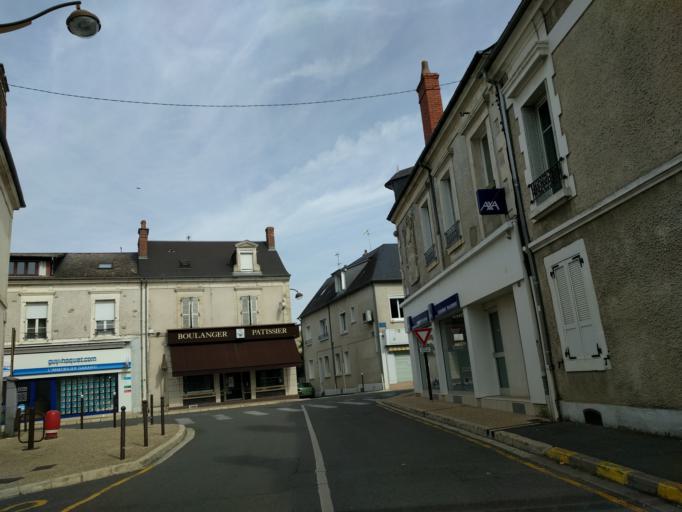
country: FR
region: Centre
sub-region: Departement du Cher
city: Bourges
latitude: 47.0766
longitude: 2.4038
